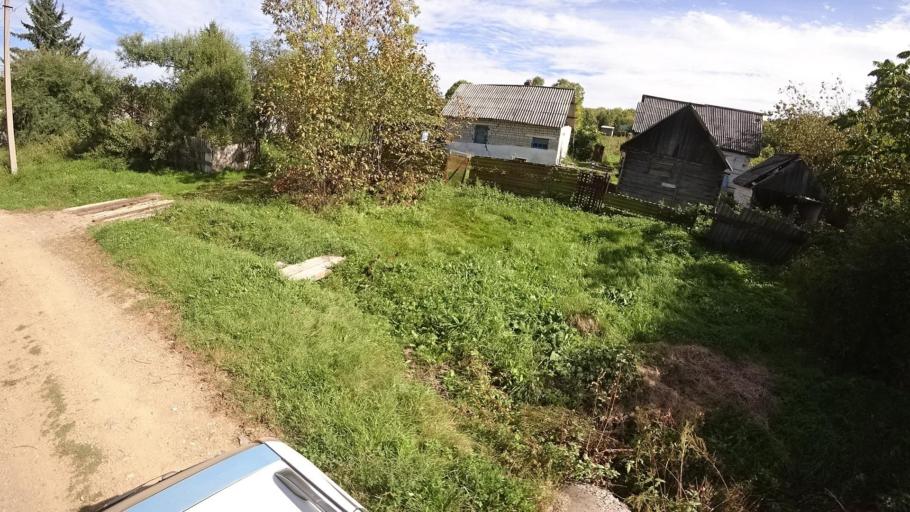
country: RU
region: Primorskiy
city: Yakovlevka
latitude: 44.3887
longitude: 133.6036
